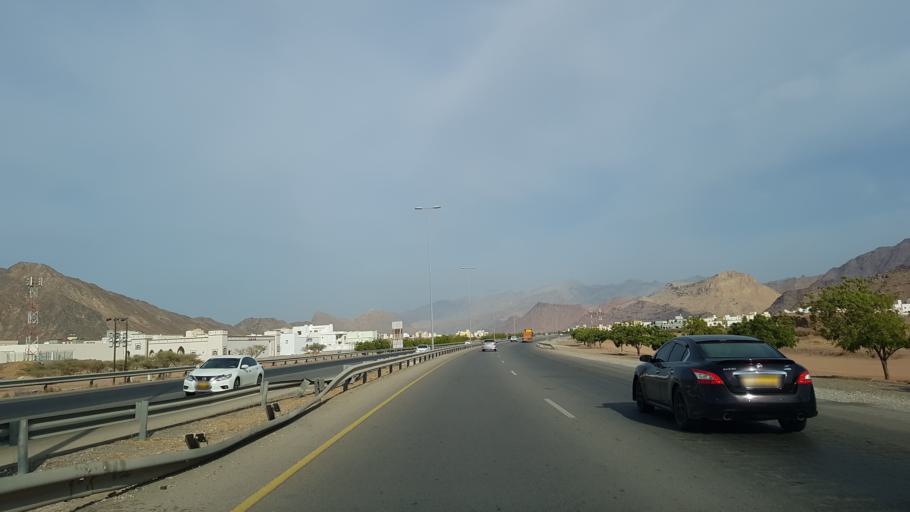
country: OM
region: Muhafazat ad Dakhiliyah
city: Bidbid
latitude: 23.4669
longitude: 58.1443
